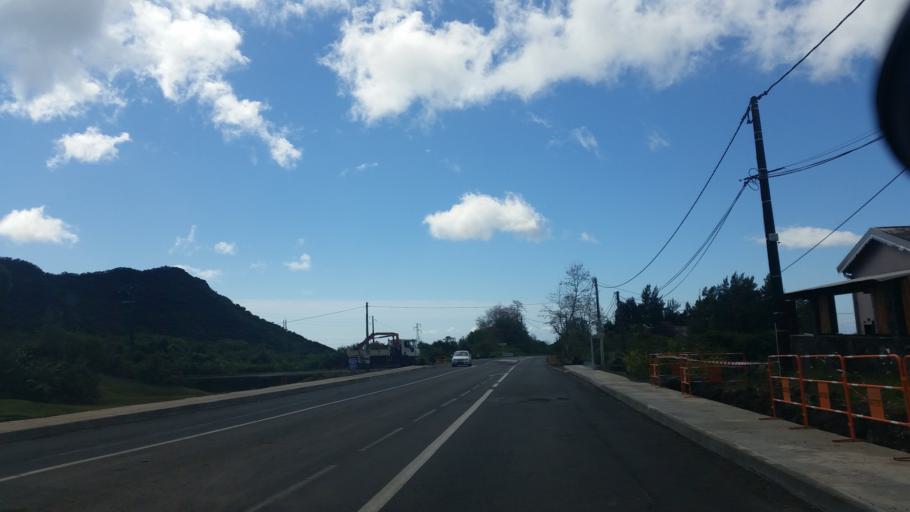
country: RE
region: Reunion
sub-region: Reunion
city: Saint-Benoit
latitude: -21.1177
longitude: 55.6461
